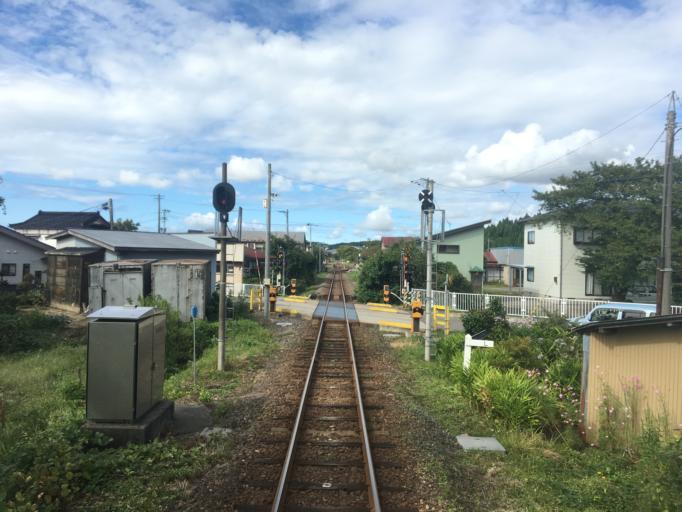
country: JP
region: Yamagata
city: Yuza
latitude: 39.3110
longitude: 140.1135
